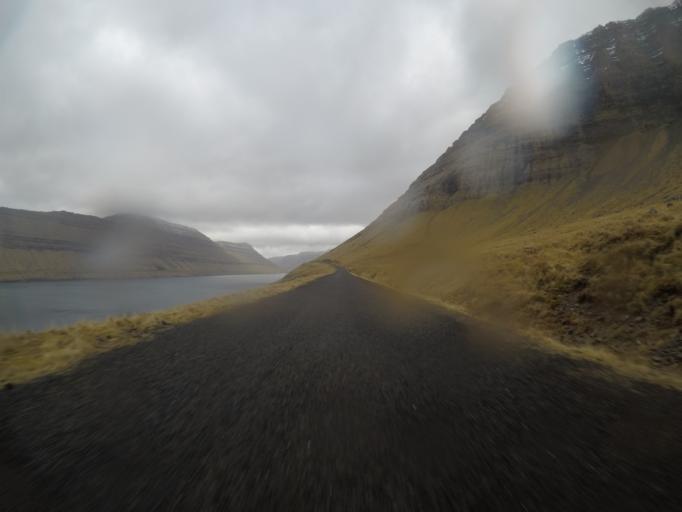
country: FO
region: Nordoyar
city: Klaksvik
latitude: 62.3342
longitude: -6.5764
